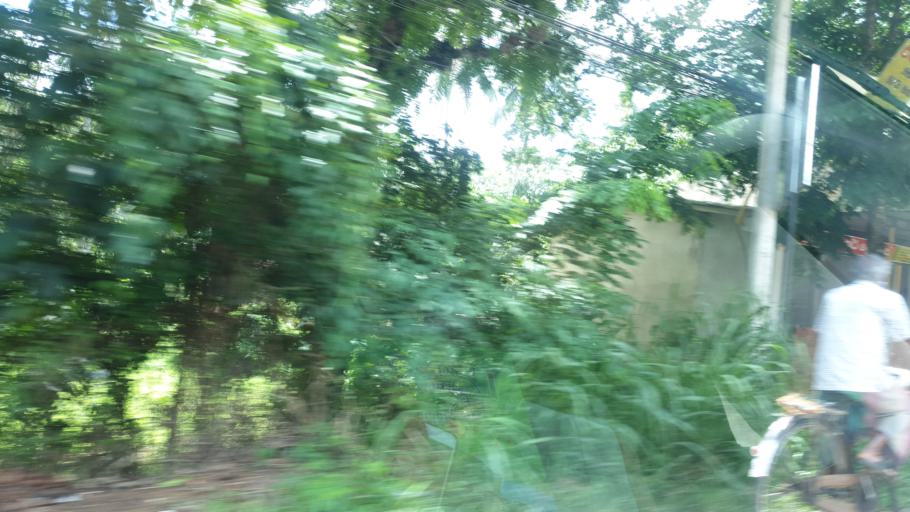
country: LK
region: Western
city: Horawala Junction
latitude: 6.5235
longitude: 80.2163
